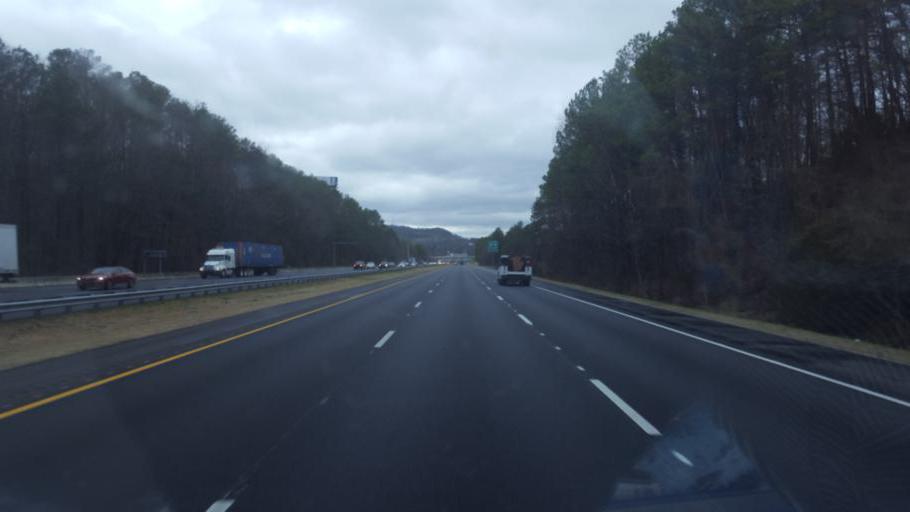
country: US
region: Georgia
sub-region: Catoosa County
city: Ringgold
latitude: 34.8867
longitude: -85.0629
